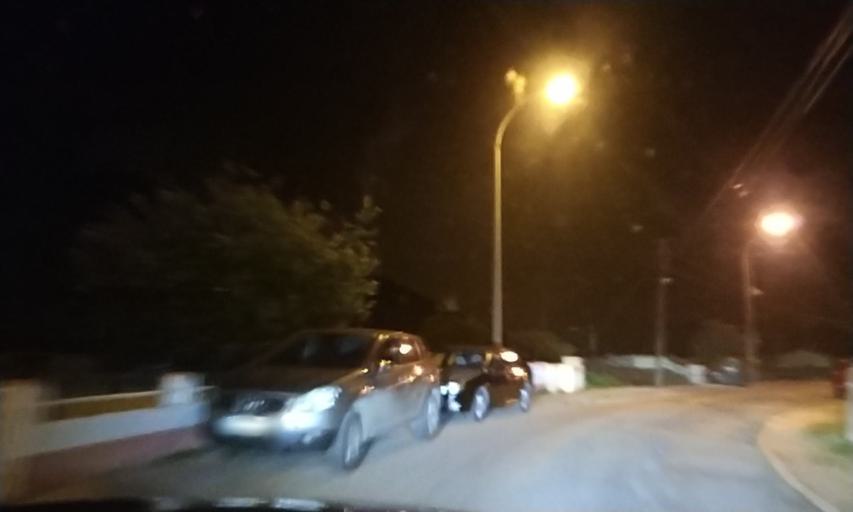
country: PT
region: Setubal
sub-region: Setubal
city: Setubal
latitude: 38.5287
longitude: -8.9049
